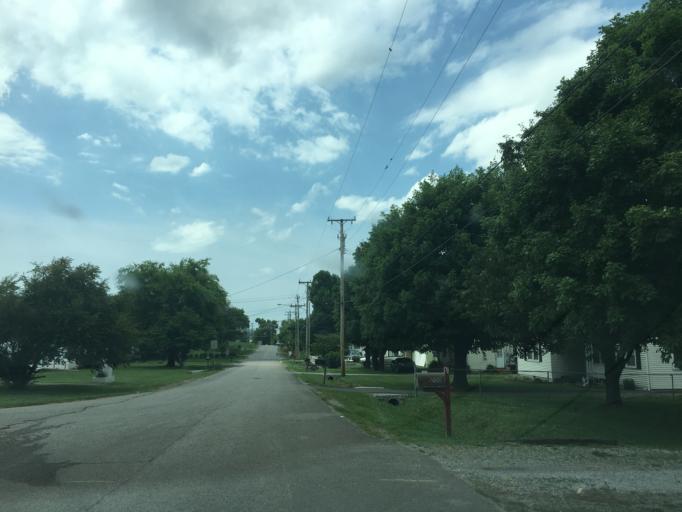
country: US
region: Tennessee
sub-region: Davidson County
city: Nashville
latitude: 36.1304
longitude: -86.7489
